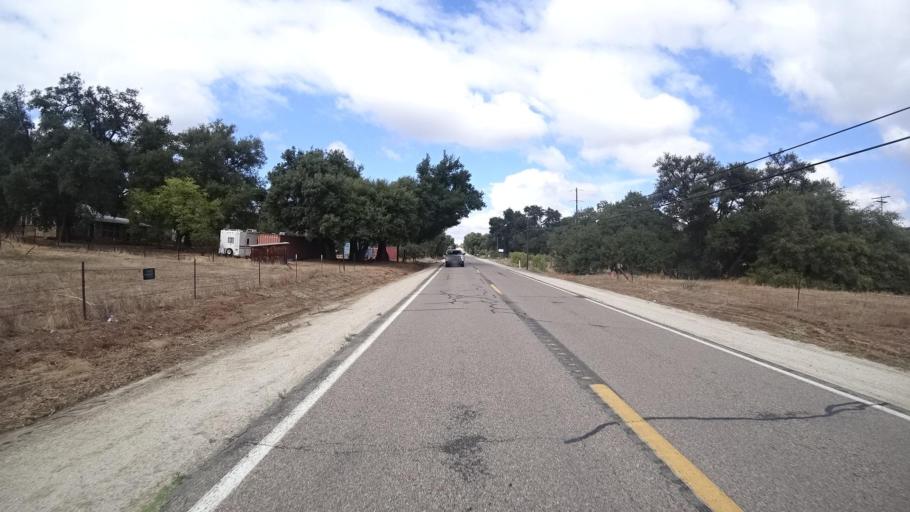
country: US
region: California
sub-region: San Diego County
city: Campo
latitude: 32.6658
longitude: -116.4882
